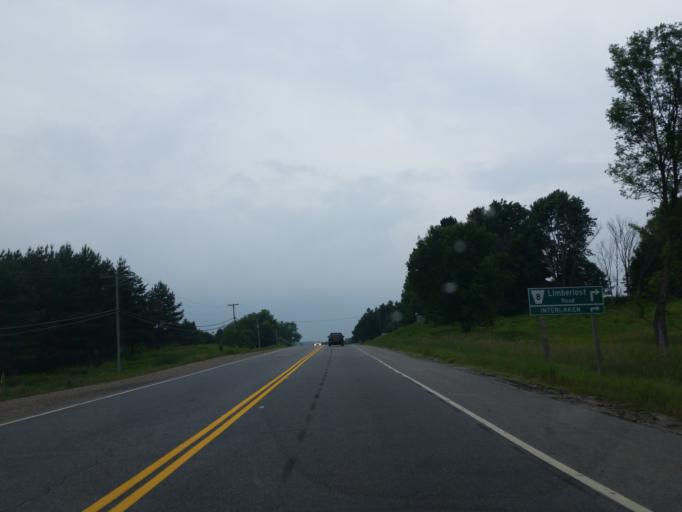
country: CA
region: Ontario
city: Huntsville
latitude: 45.3553
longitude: -79.0920
